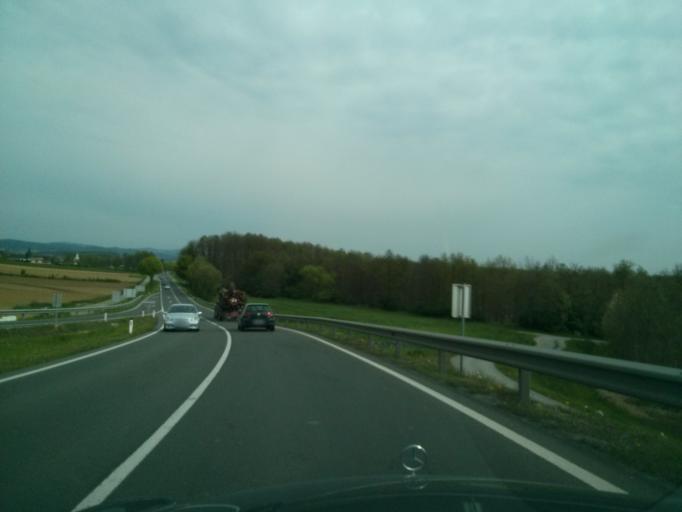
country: AT
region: Burgenland
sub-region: Politischer Bezirk Oberwart
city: Oberwart
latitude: 47.3040
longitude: 16.2067
